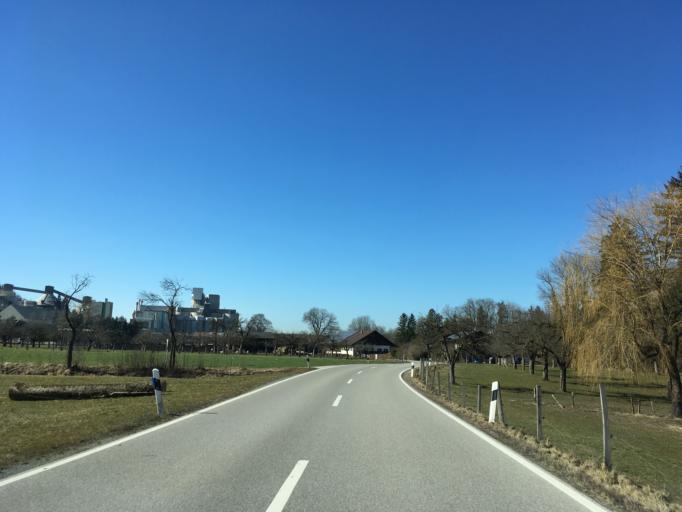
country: DE
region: Bavaria
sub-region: Upper Bavaria
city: Samerberg
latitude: 47.7928
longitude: 12.1901
